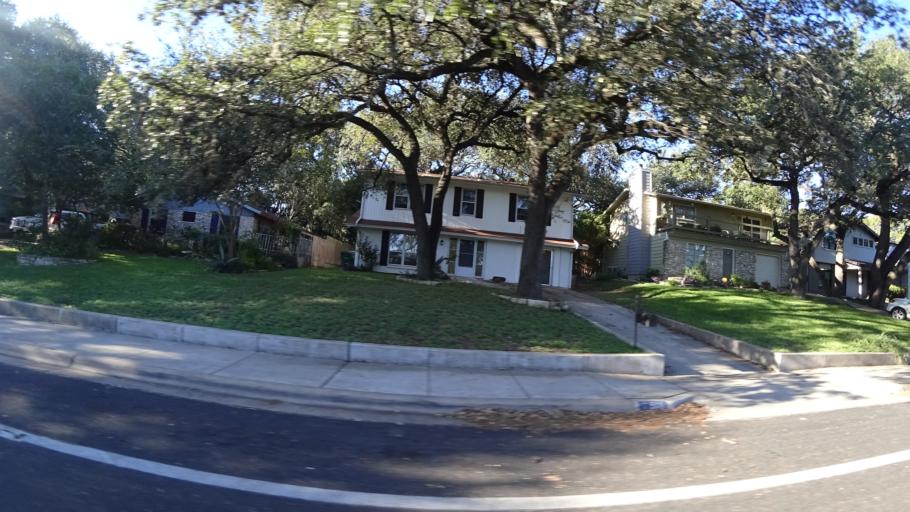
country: US
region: Texas
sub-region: Travis County
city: Austin
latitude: 30.2318
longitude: -97.7647
